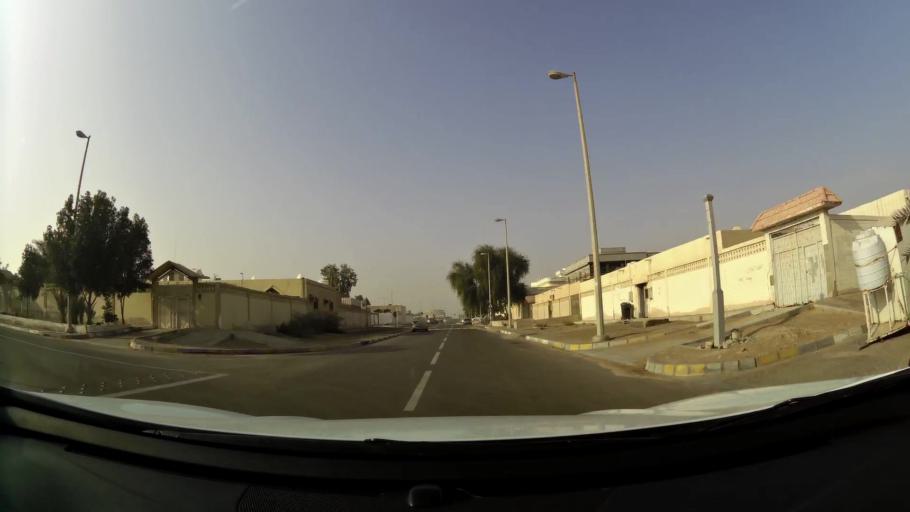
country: AE
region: Abu Dhabi
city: Abu Dhabi
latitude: 24.2766
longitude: 54.6459
